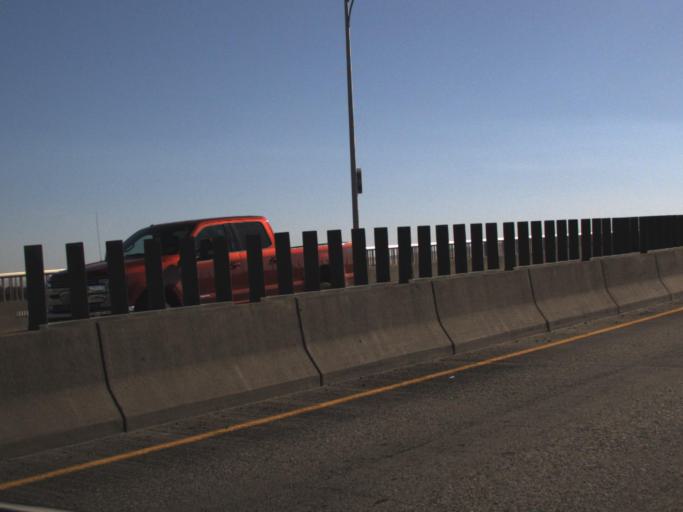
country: US
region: Washington
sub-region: Benton County
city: Kennewick
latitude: 46.2275
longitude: -119.1348
